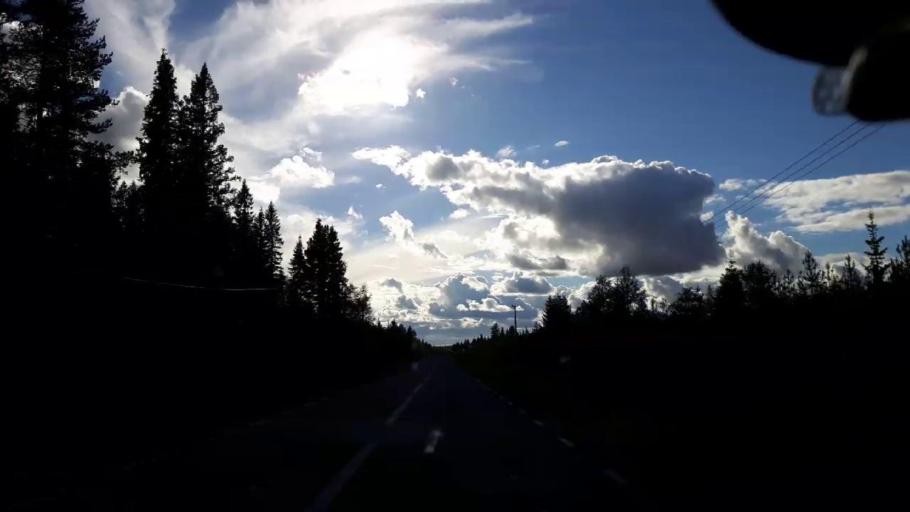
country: SE
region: Jaemtland
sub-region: Stroemsunds Kommun
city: Stroemsund
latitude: 63.5528
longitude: 15.5176
